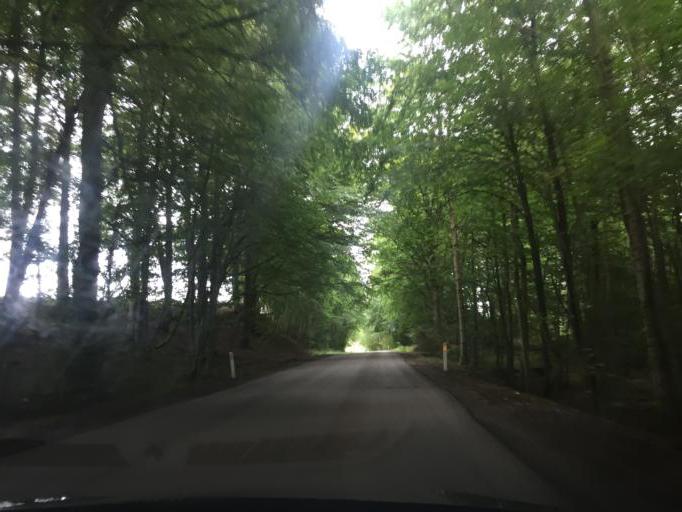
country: DK
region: South Denmark
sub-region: Assens Kommune
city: Tommerup Stationsby
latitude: 55.3543
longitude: 10.1881
